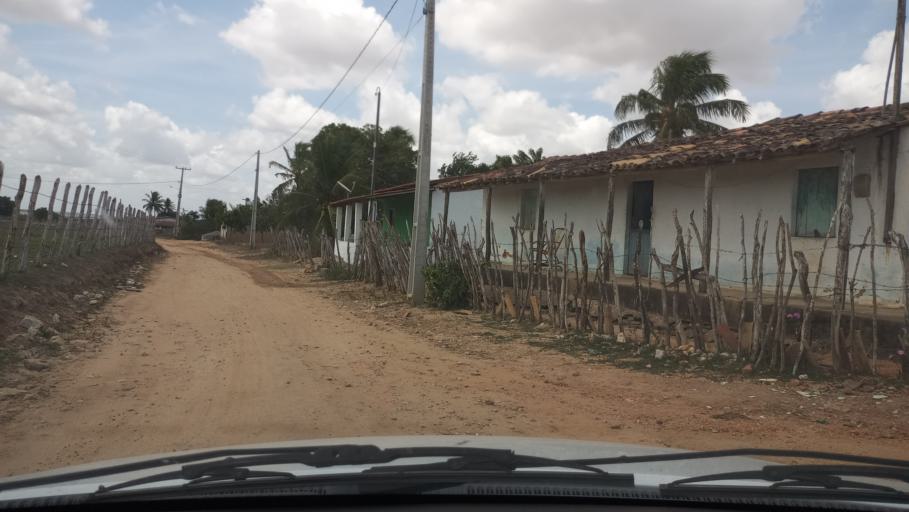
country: BR
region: Rio Grande do Norte
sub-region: Brejinho
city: Brejinho
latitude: -6.2732
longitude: -35.3471
